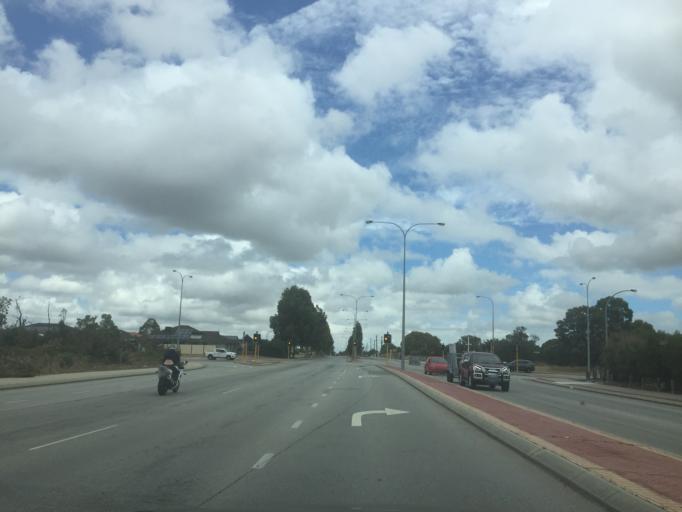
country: AU
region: Western Australia
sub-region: Gosnells
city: Thornlie
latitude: -32.0823
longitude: 115.9524
